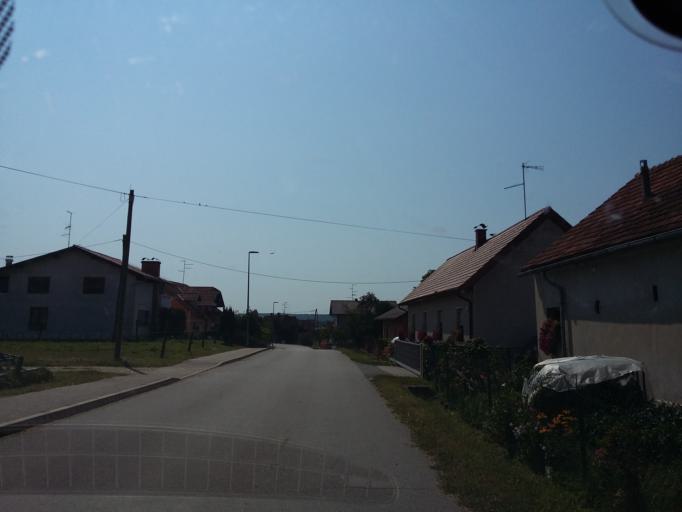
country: SI
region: Hodos-Hodos
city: Hodos
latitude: 46.8333
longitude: 16.3185
